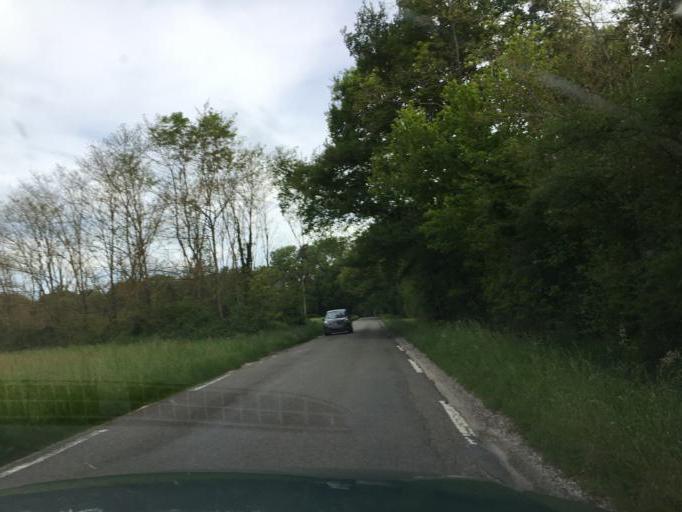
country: FR
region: Centre
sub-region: Departement du Loiret
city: Chaingy
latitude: 47.9163
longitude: 1.7866
